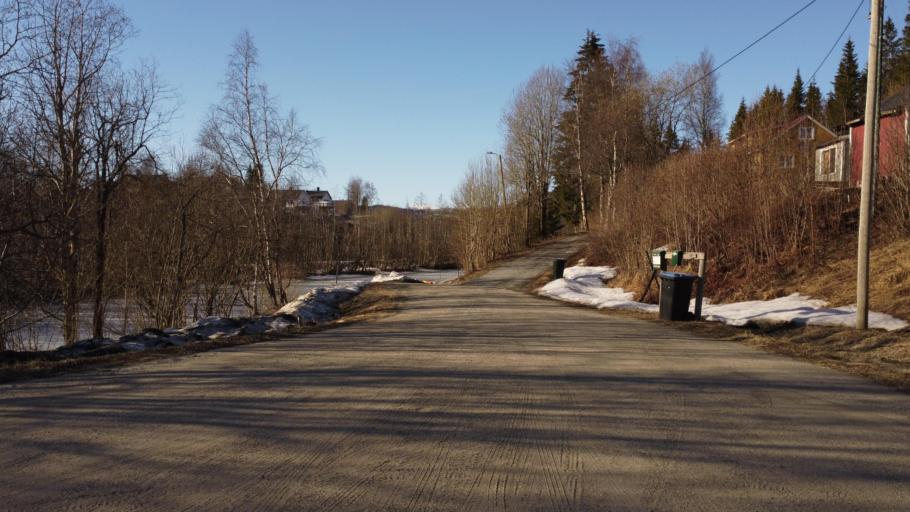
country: NO
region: Nordland
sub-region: Rana
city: Mo i Rana
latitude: 66.3166
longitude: 14.1703
